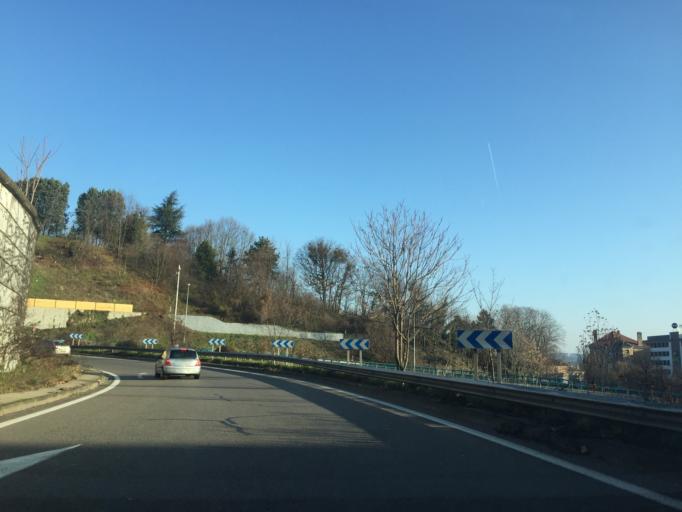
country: FR
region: Rhone-Alpes
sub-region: Departement du Rhone
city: Ecully
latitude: 45.7721
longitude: 4.7892
